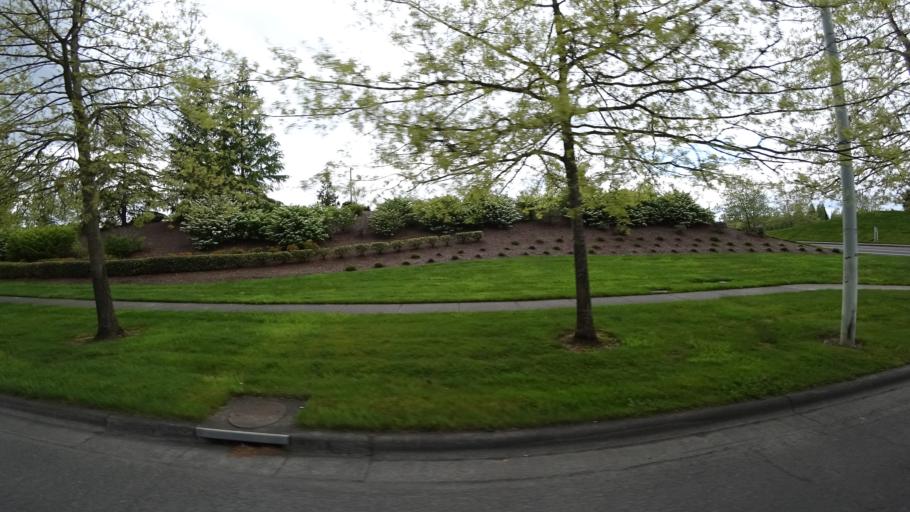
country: US
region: Oregon
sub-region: Washington County
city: Rockcreek
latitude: 45.5408
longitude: -122.9075
